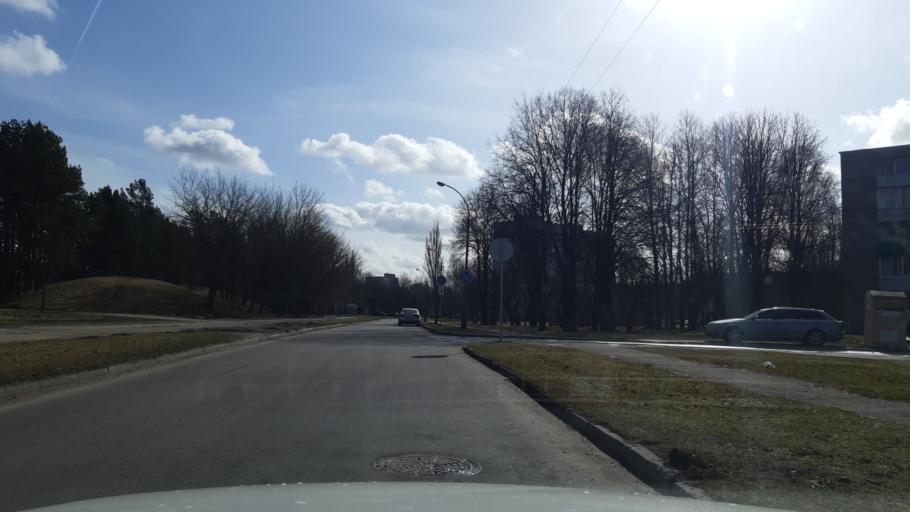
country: LT
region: Kauno apskritis
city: Dainava (Kaunas)
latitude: 54.9163
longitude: 23.9671
